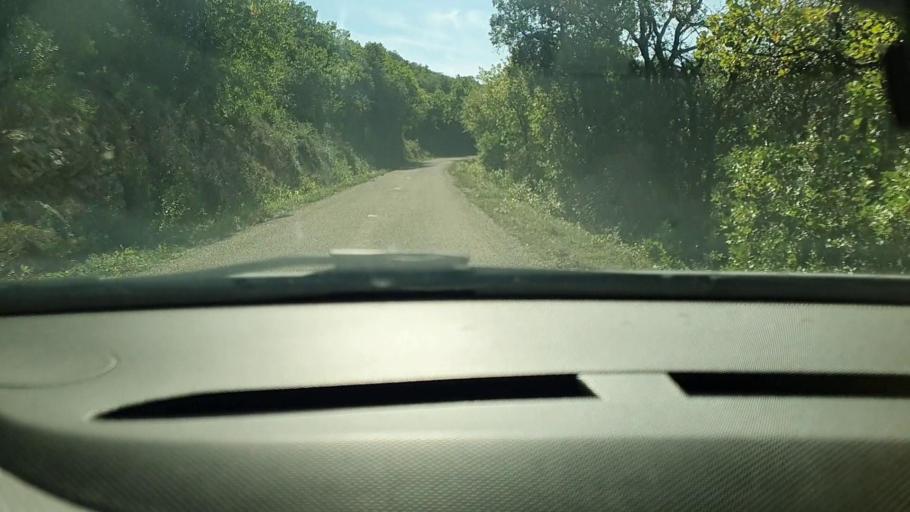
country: FR
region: Languedoc-Roussillon
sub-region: Departement du Gard
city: Barjac
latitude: 44.2026
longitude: 4.3135
